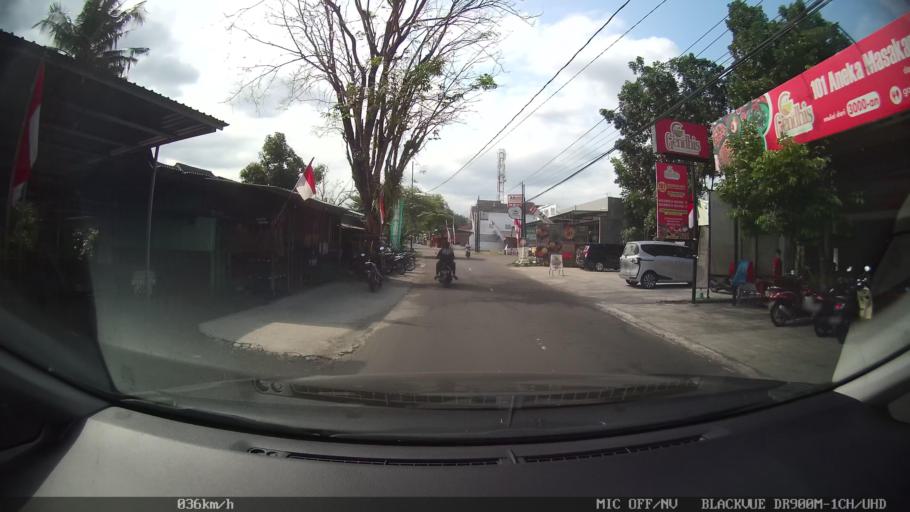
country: ID
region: Daerah Istimewa Yogyakarta
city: Depok
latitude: -7.7384
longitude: 110.4208
